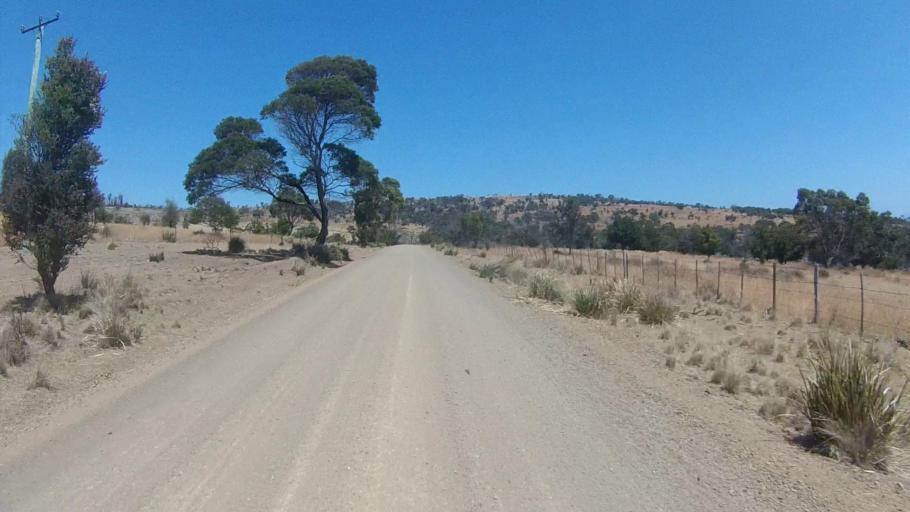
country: AU
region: Tasmania
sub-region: Sorell
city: Sorell
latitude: -42.8936
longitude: 147.8415
